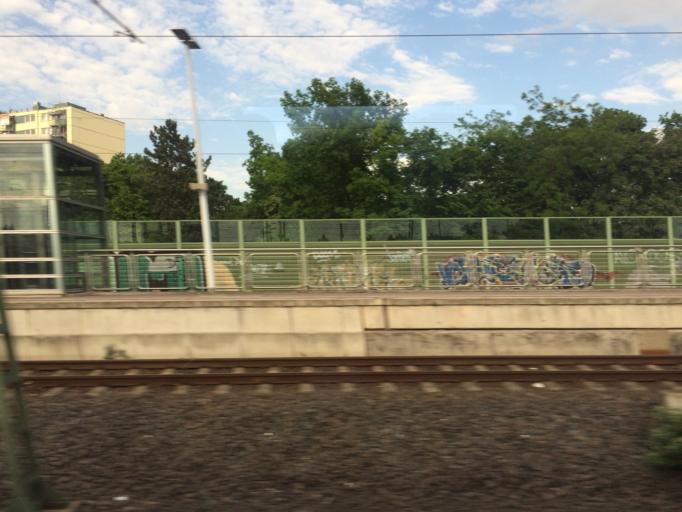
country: DE
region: North Rhine-Westphalia
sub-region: Regierungsbezirk Koln
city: Gremberghoven
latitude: 50.8948
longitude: 7.0574
